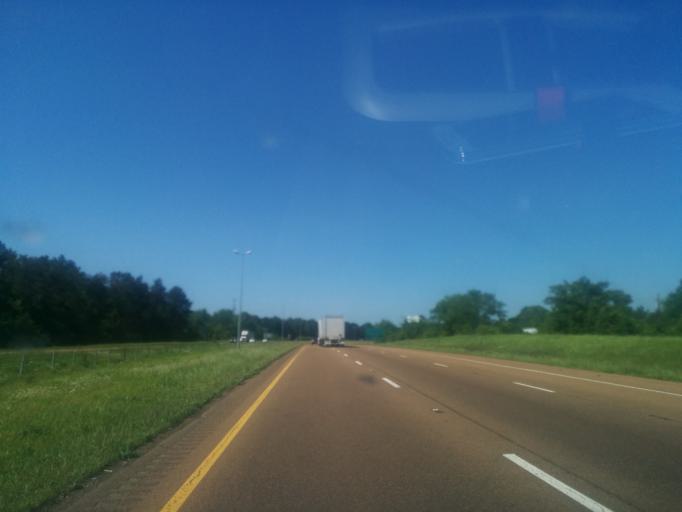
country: US
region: Mississippi
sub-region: Hinds County
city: Clinton
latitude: 32.3464
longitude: -90.2455
